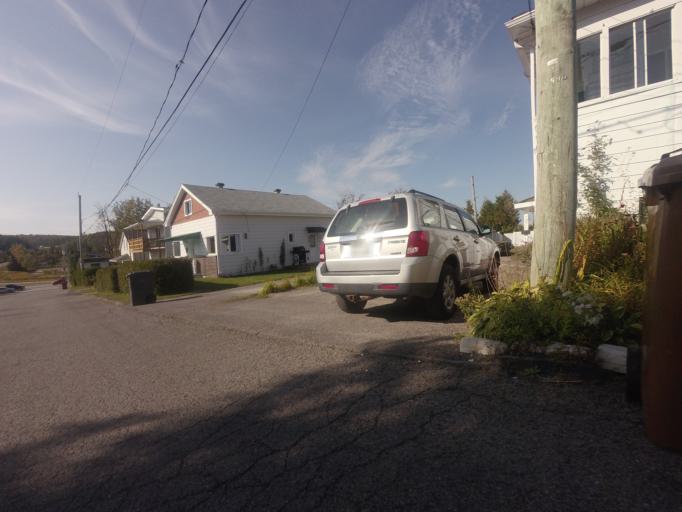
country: CA
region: Quebec
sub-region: Laurentides
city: Sainte-Agathe-des-Monts
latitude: 46.0448
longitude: -74.2684
